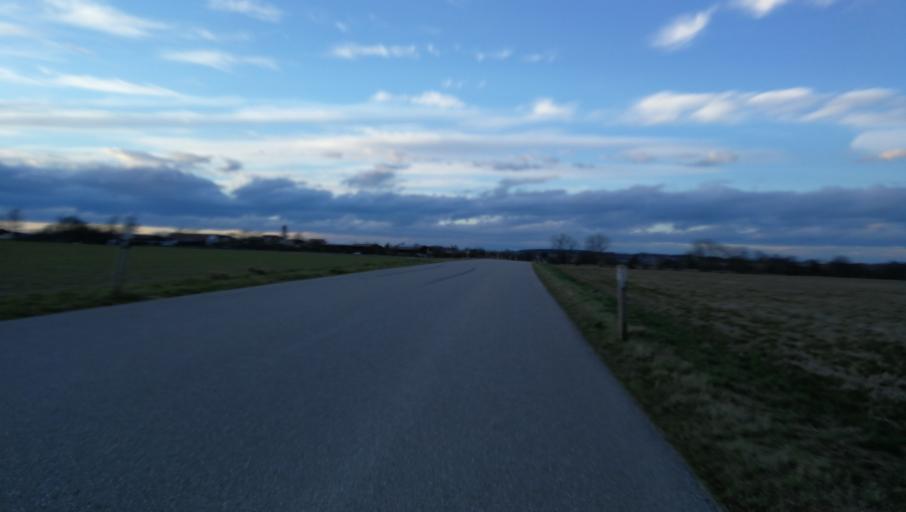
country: DE
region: Bavaria
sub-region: Upper Bavaria
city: Fuerstenfeldbruck
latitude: 48.2058
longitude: 11.2274
